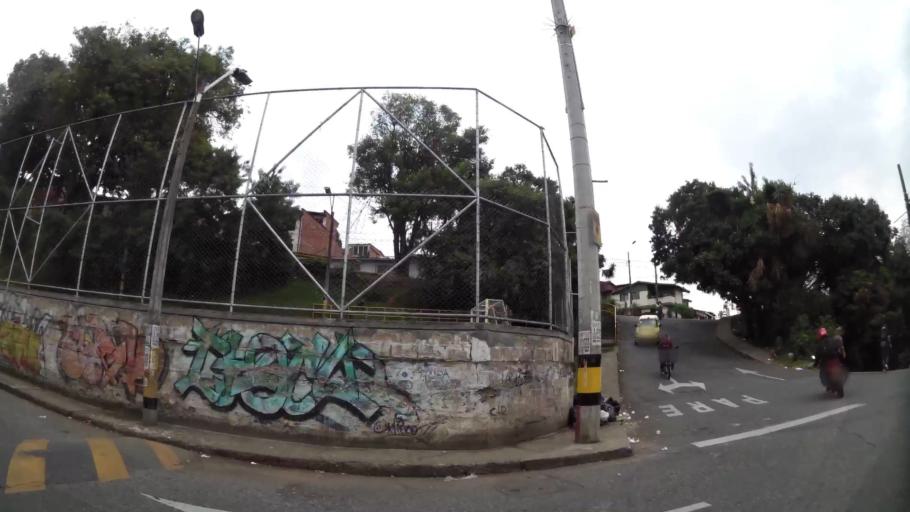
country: CO
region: Antioquia
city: Medellin
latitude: 6.2463
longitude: -75.5525
